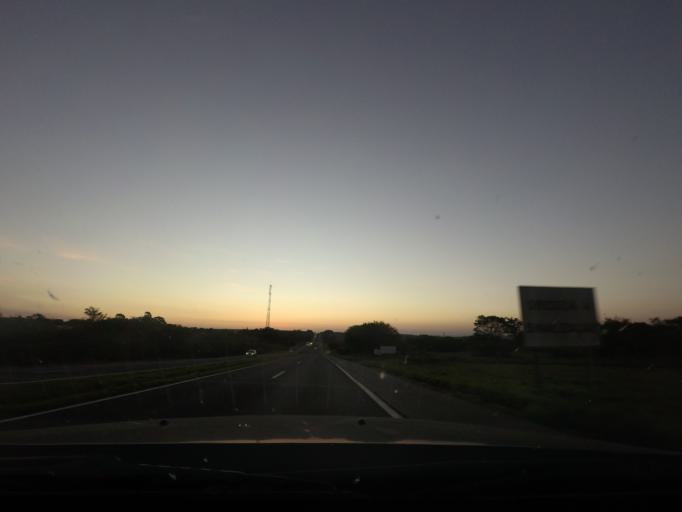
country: BR
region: Sao Paulo
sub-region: Piracicaba
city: Piracicaba
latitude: -22.7266
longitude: -47.5546
